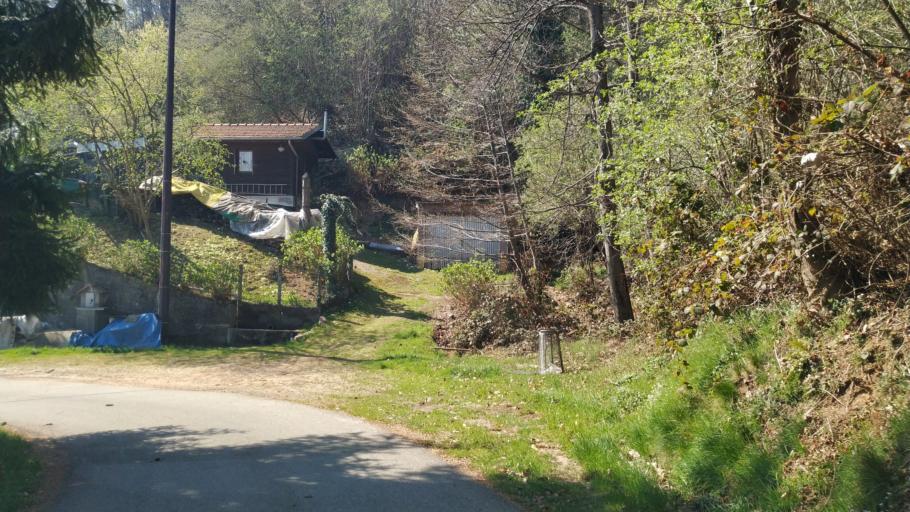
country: IT
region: Piedmont
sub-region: Provincia di Biella
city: Frazione Chiesa
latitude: 45.6883
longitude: 8.2004
